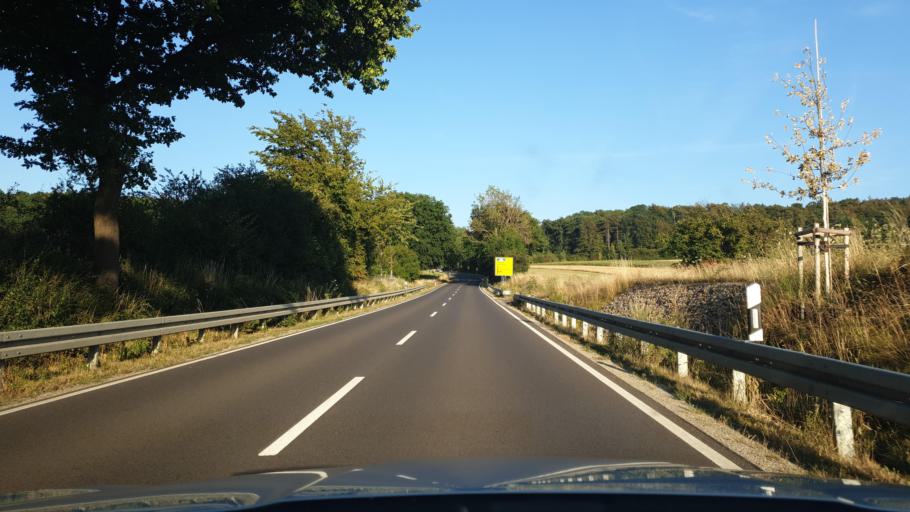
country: DE
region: Lower Saxony
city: Heuerssen
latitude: 52.3164
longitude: 9.2717
